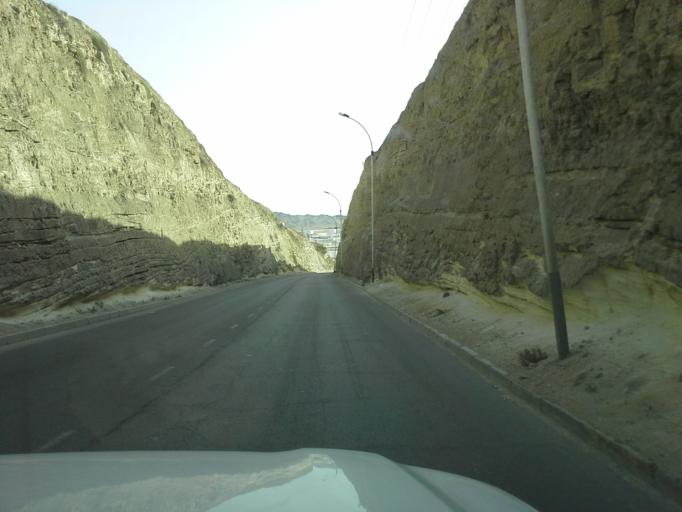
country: TM
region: Balkan
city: Turkmenbasy
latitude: 40.0386
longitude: 52.9707
